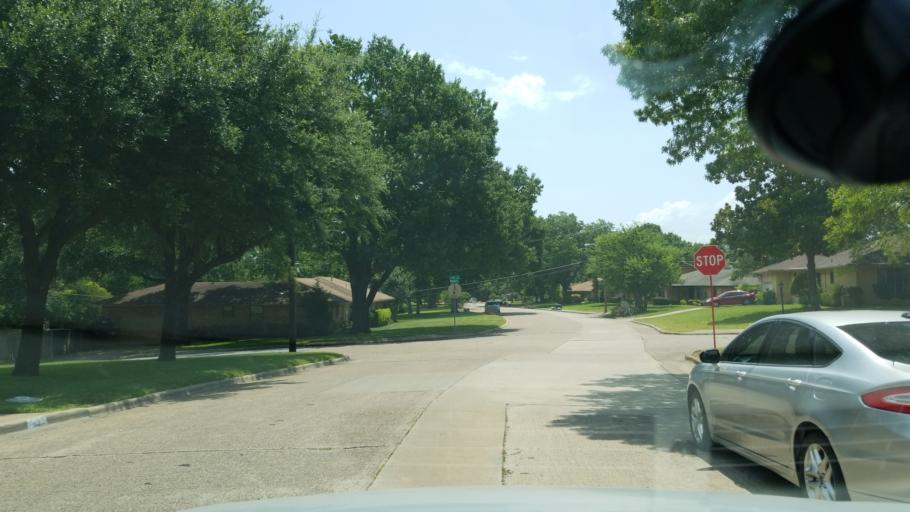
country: US
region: Texas
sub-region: Dallas County
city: Cockrell Hill
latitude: 32.6820
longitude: -96.8352
